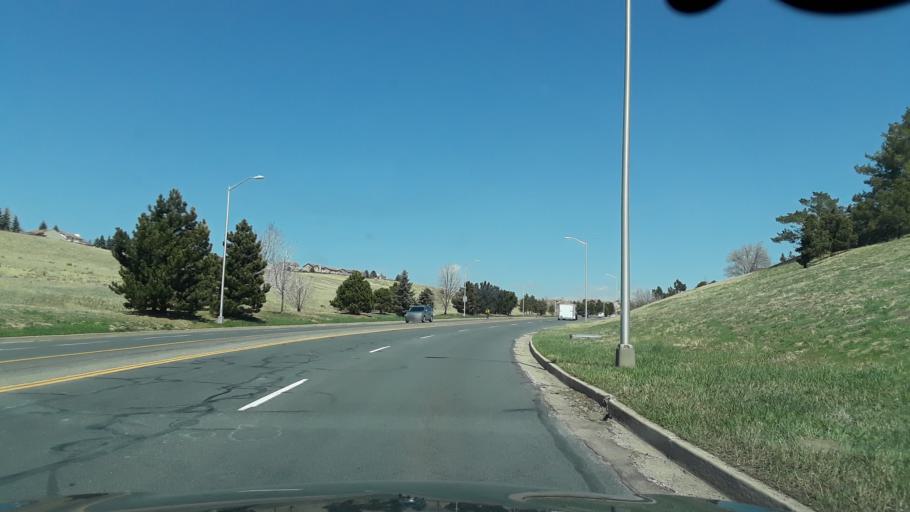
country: US
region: Colorado
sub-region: El Paso County
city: Black Forest
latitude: 38.9473
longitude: -104.7428
